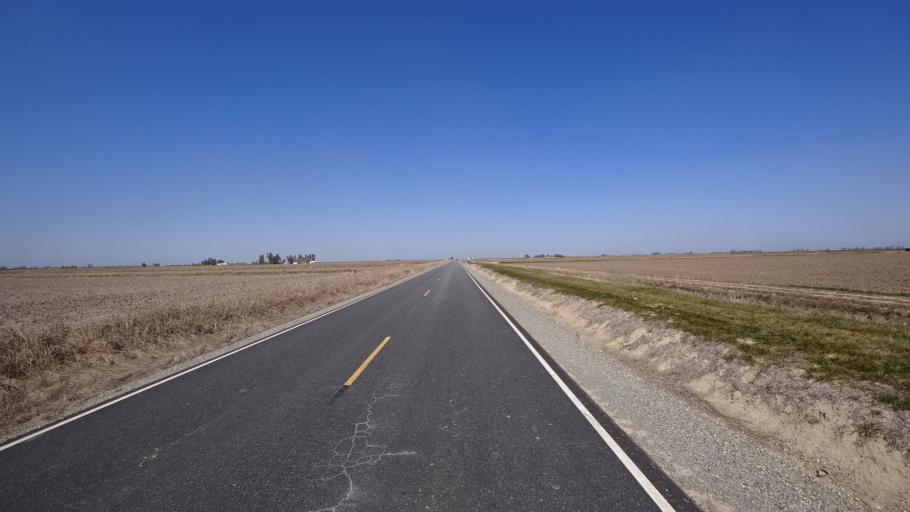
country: US
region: California
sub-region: Glenn County
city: Willows
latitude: 39.5462
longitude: -122.1369
